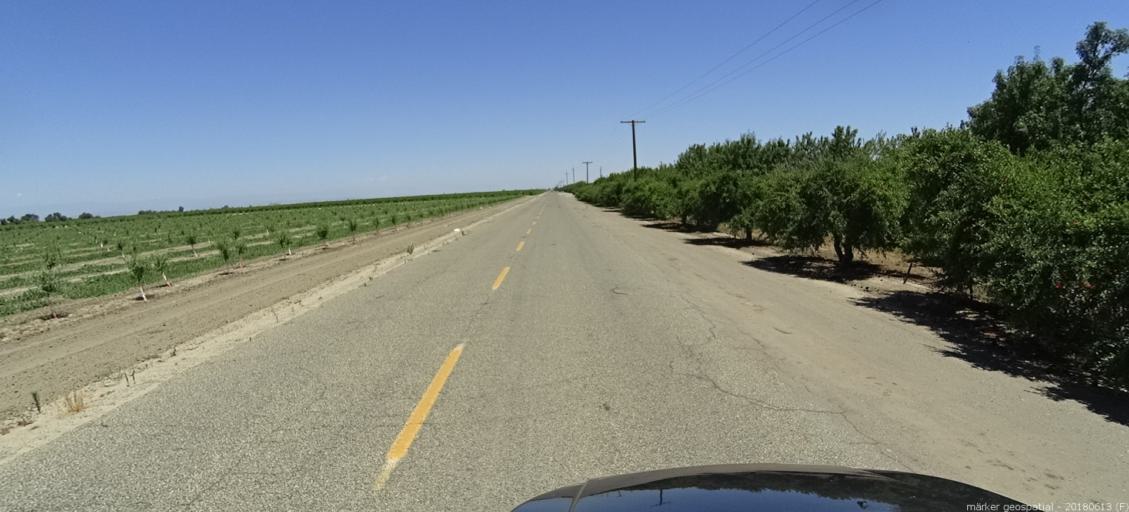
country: US
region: California
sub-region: Madera County
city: Fairmead
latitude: 36.9964
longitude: -120.1591
